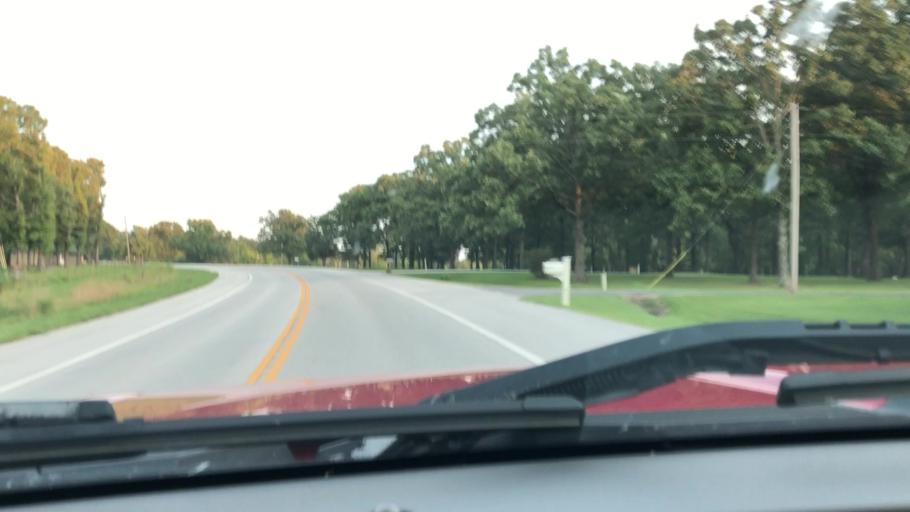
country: US
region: Missouri
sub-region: Jasper County
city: Duquesne
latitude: 36.9791
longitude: -94.4641
